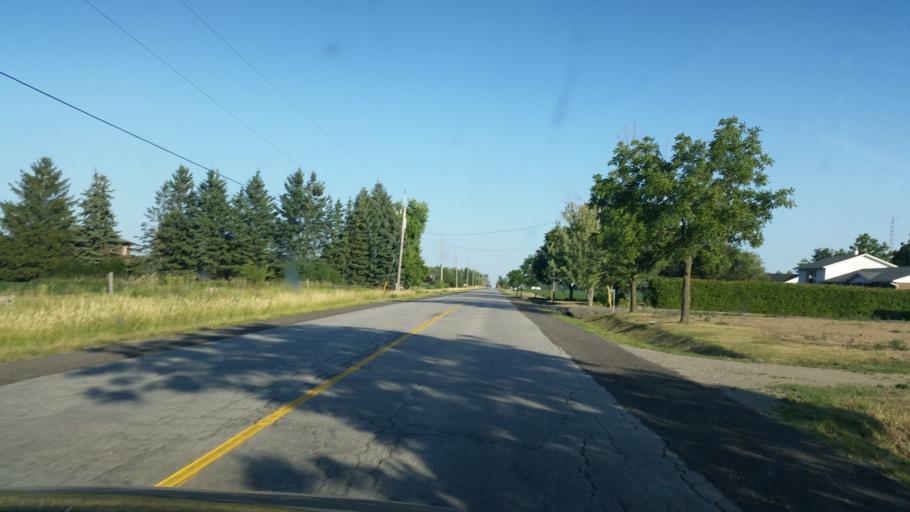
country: CA
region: Ontario
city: Brampton
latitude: 43.7657
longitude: -79.8208
